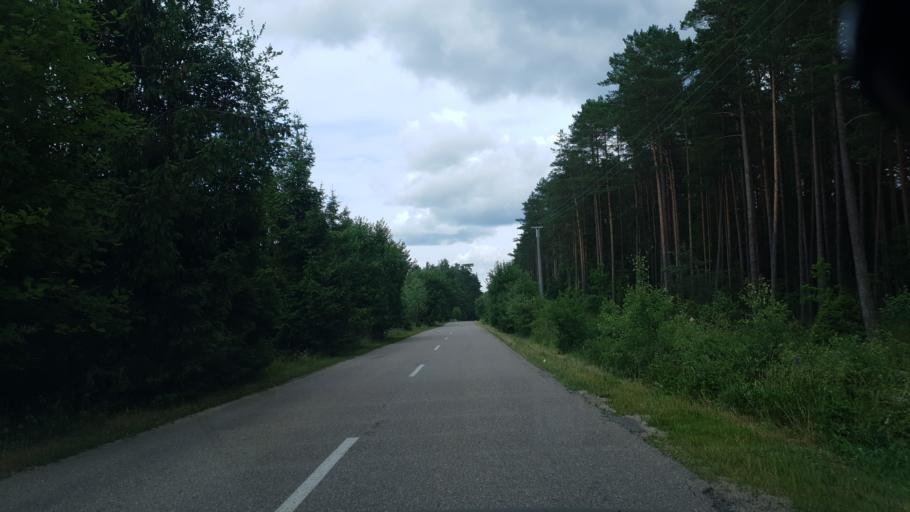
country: PL
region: Pomeranian Voivodeship
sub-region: Powiat kartuski
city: Stezyca
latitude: 54.2489
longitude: 18.0051
